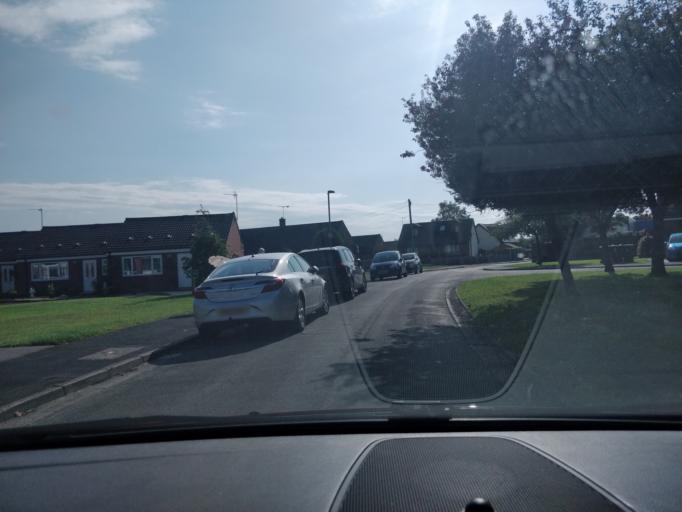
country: GB
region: England
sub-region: Lancashire
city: Banks
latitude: 53.6789
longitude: -2.9219
